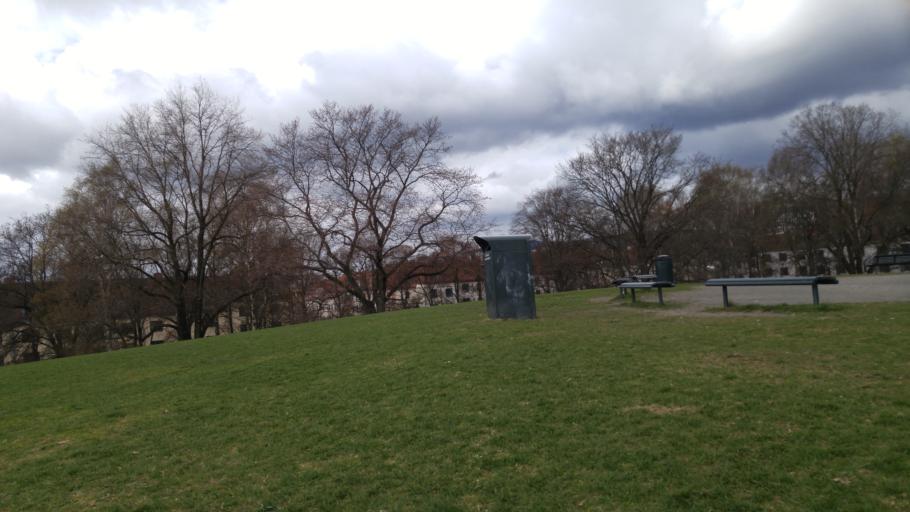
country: NO
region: Oslo
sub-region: Oslo
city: Oslo
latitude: 59.9353
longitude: 10.7708
